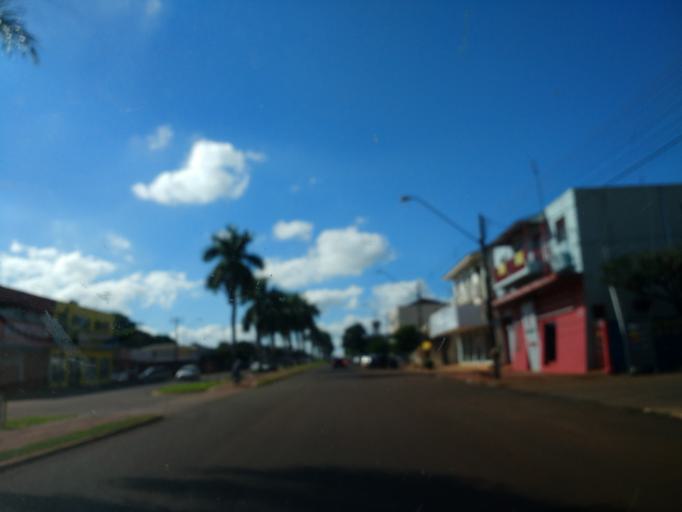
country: BR
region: Parana
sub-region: Palotina
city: Palotina
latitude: -24.4022
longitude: -53.5132
